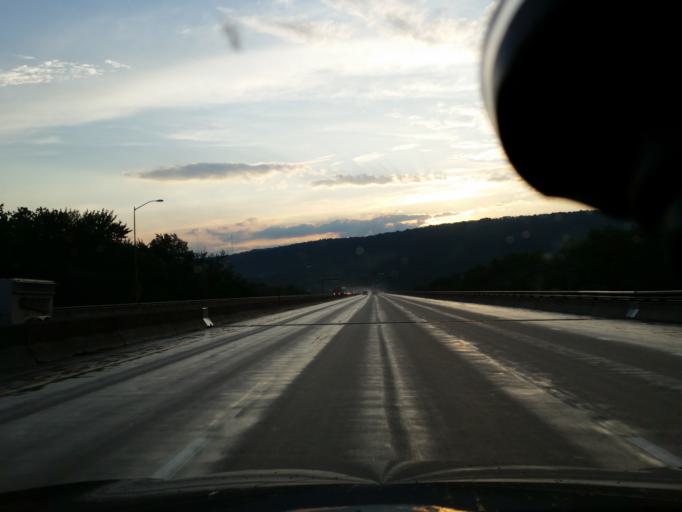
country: US
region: Pennsylvania
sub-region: Cumberland County
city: Enola
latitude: 40.3128
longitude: -76.9046
